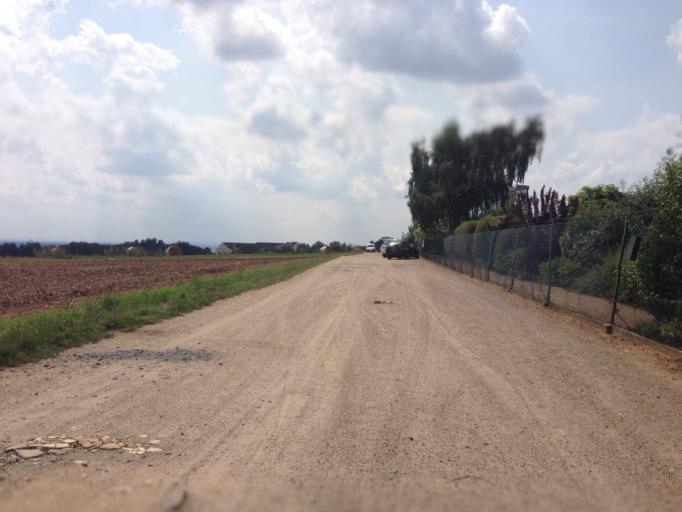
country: DE
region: Hesse
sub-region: Regierungsbezirk Darmstadt
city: Bad Vilbel
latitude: 50.1628
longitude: 8.7696
